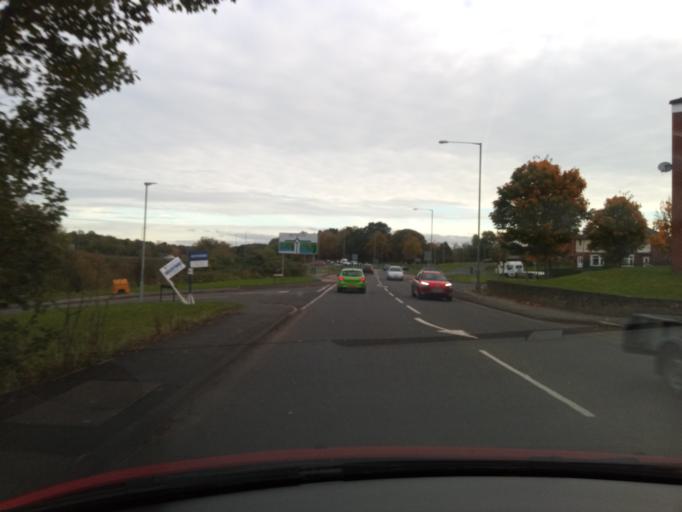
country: GB
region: England
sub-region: County Durham
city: Bishop Auckland
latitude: 54.6542
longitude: -1.6688
